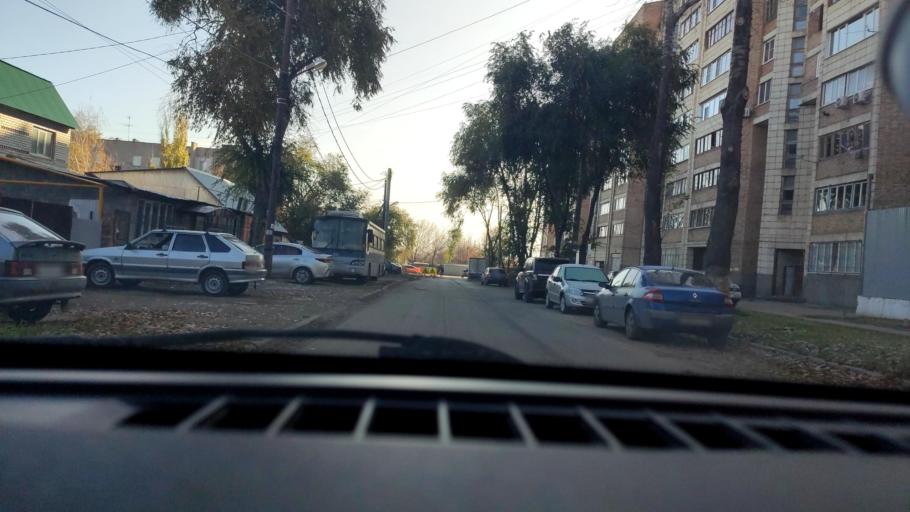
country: RU
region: Samara
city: Samara
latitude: 53.1896
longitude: 50.2178
